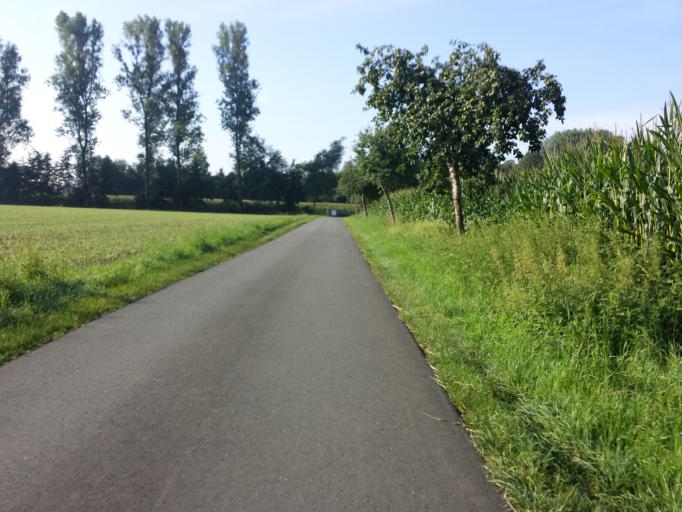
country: DE
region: North Rhine-Westphalia
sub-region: Regierungsbezirk Detmold
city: Guetersloh
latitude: 51.9353
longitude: 8.3161
